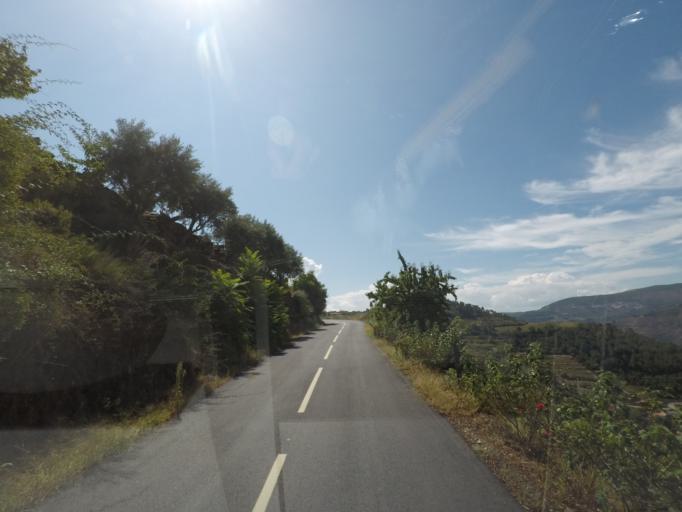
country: PT
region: Vila Real
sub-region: Sabrosa
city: Sabrosa
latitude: 41.2212
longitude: -7.5254
